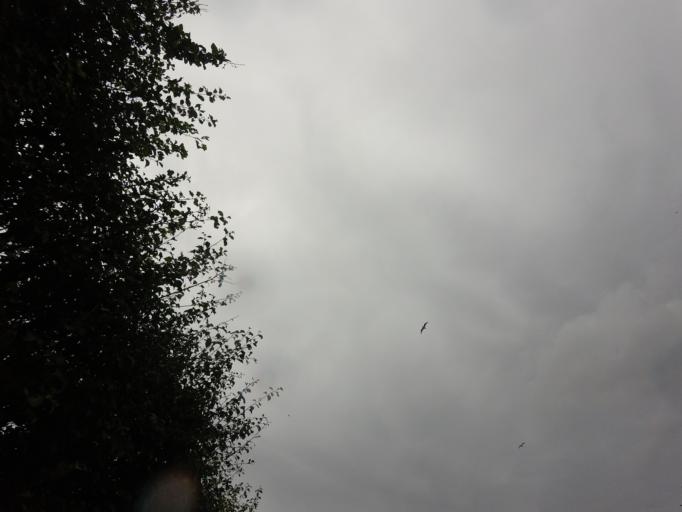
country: GB
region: England
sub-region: Cambridgeshire
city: Duxford
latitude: 52.0549
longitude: 0.1279
